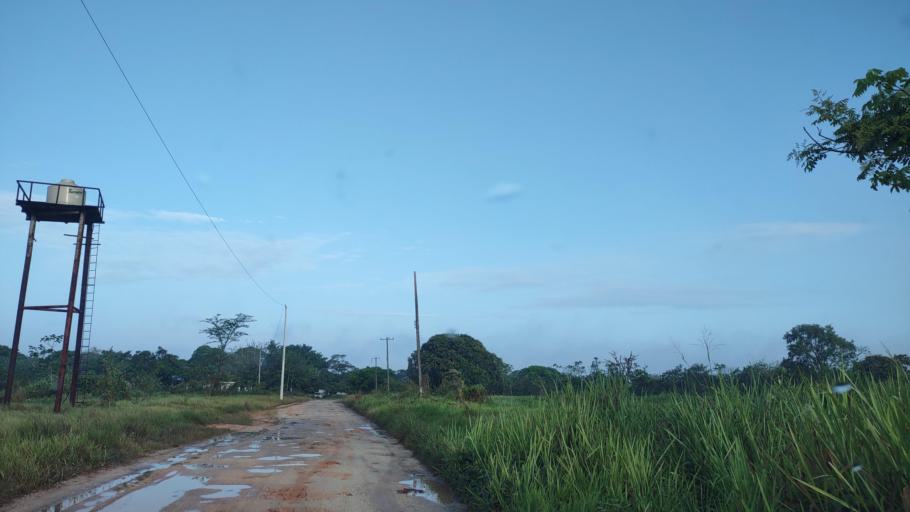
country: MX
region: Veracruz
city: Las Choapas
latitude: 17.8791
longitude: -94.1049
